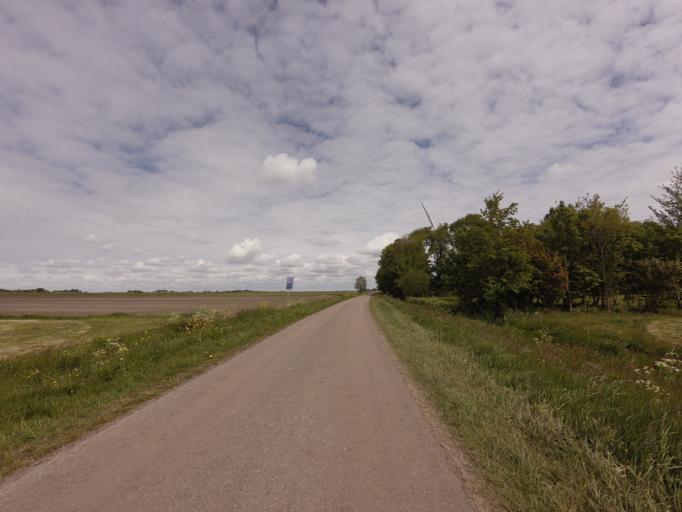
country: NL
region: Friesland
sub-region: Sudwest Fryslan
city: Koudum
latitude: 52.9153
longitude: 5.5141
